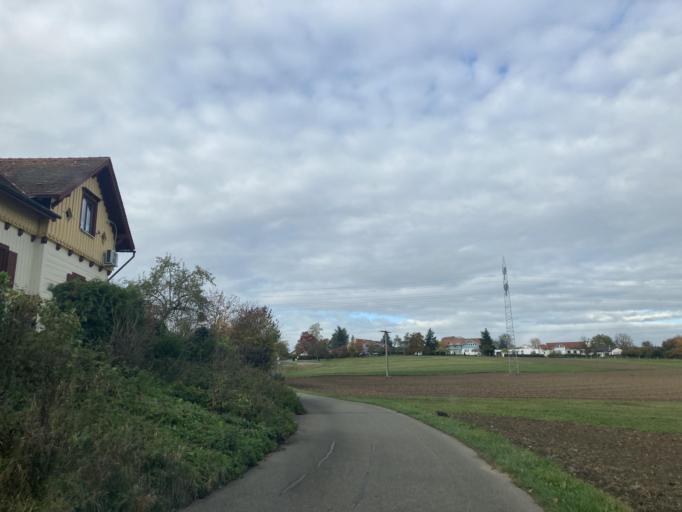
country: DE
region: Baden-Wuerttemberg
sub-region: Tuebingen Region
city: Dusslingen
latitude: 48.4512
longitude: 9.0718
